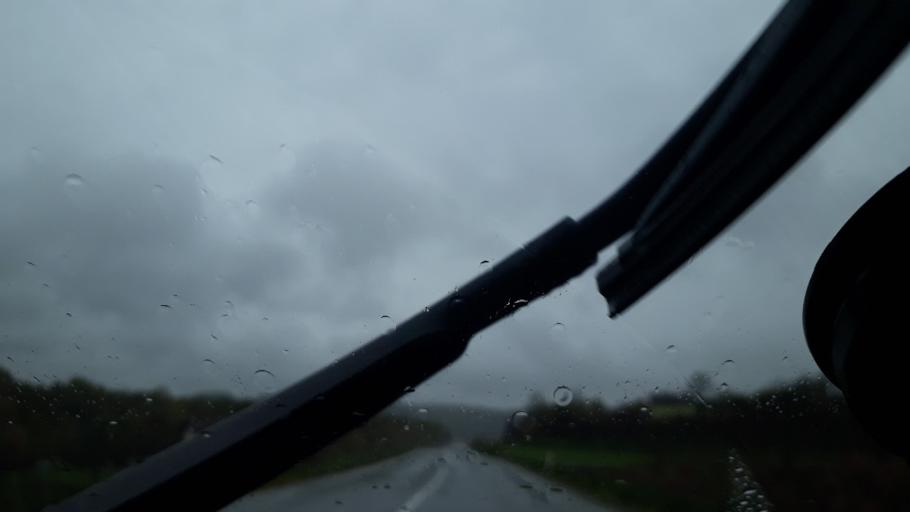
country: BA
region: Republika Srpska
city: Maglajani
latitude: 44.8646
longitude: 17.4637
